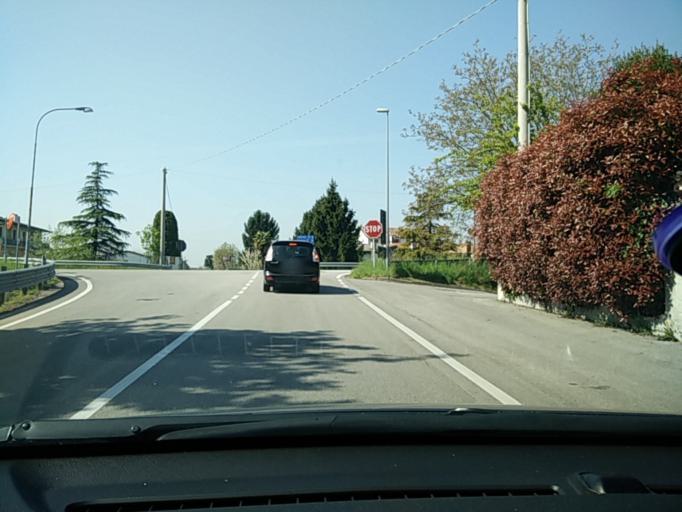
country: IT
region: Veneto
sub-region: Provincia di Treviso
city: Zenson di Piave
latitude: 45.6752
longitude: 12.4926
